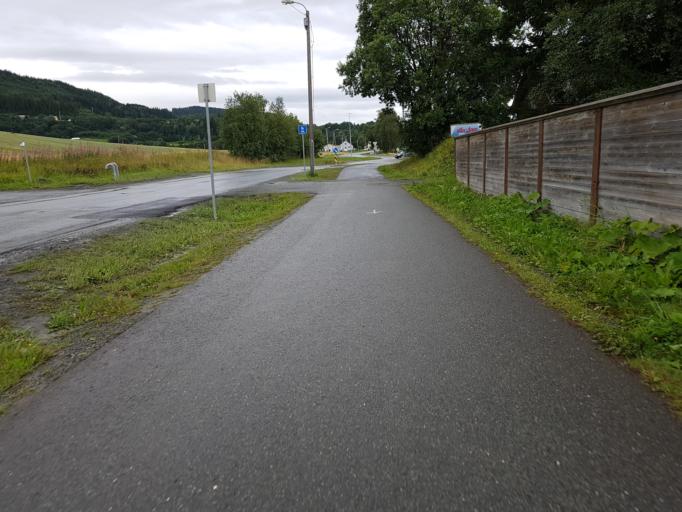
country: NO
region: Sor-Trondelag
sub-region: Trondheim
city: Trondheim
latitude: 63.3835
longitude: 10.4349
